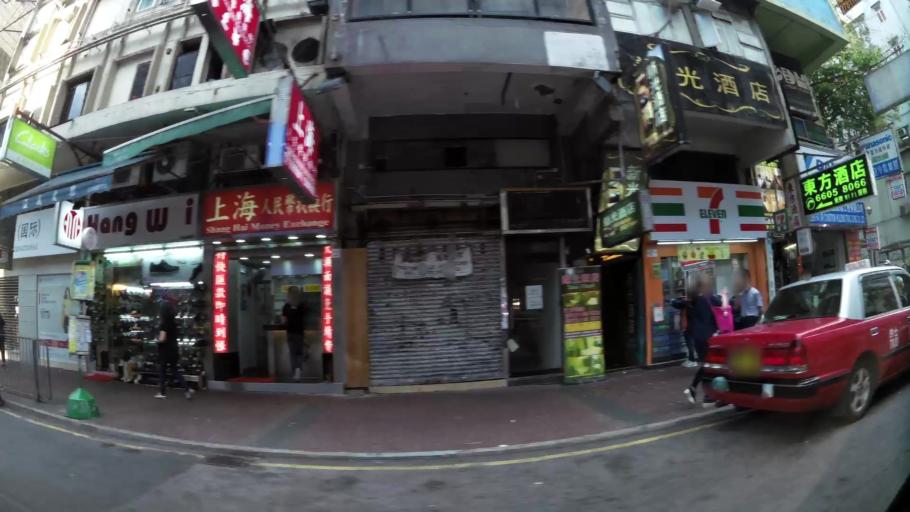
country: HK
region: Kowloon City
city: Kowloon
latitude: 22.3171
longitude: 114.1685
